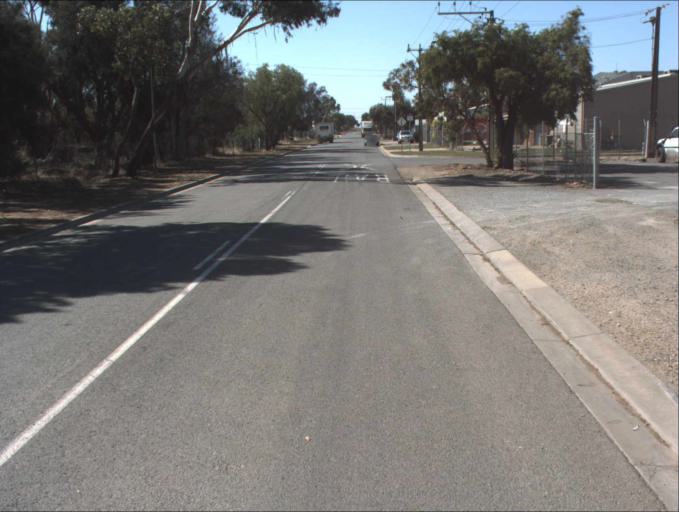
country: AU
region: South Australia
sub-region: Port Adelaide Enfield
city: Enfield
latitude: -34.8380
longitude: 138.5817
